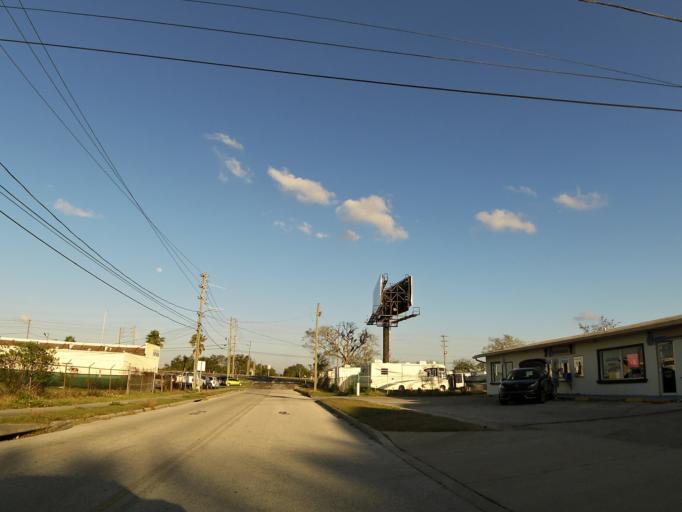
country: US
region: Florida
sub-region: Pinellas County
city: Tarpon Springs
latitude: 28.1542
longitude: -82.7419
